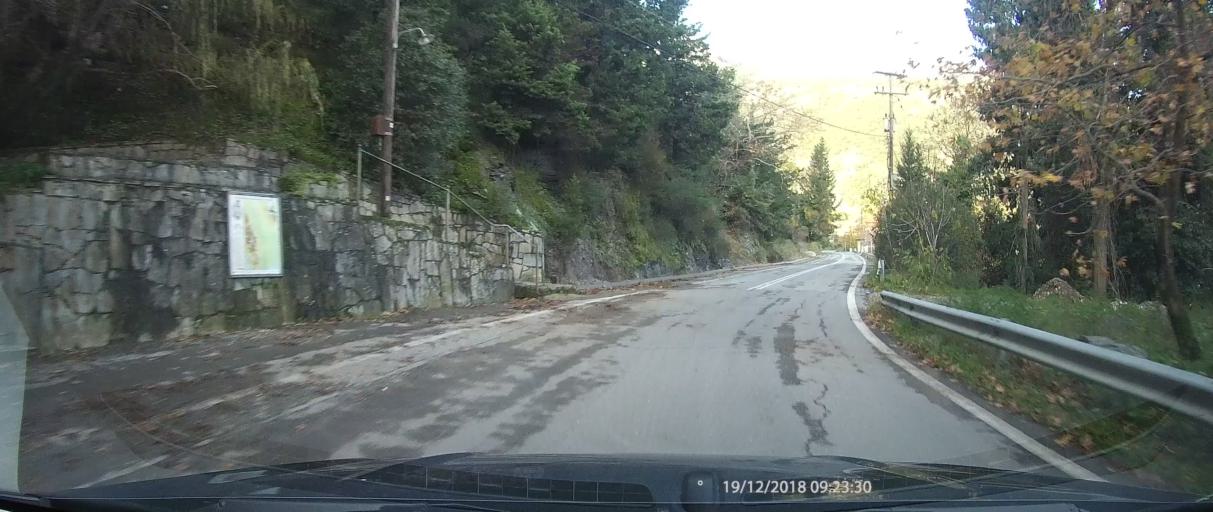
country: GR
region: Peloponnese
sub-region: Nomos Lakonias
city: Magoula
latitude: 37.0938
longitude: 22.3470
